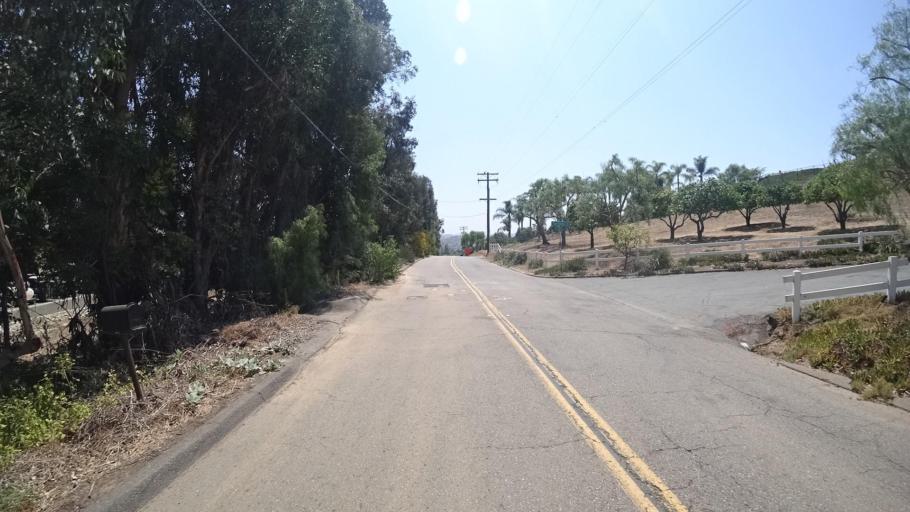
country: US
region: California
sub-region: San Diego County
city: Bonsall
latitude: 33.3152
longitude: -117.2068
